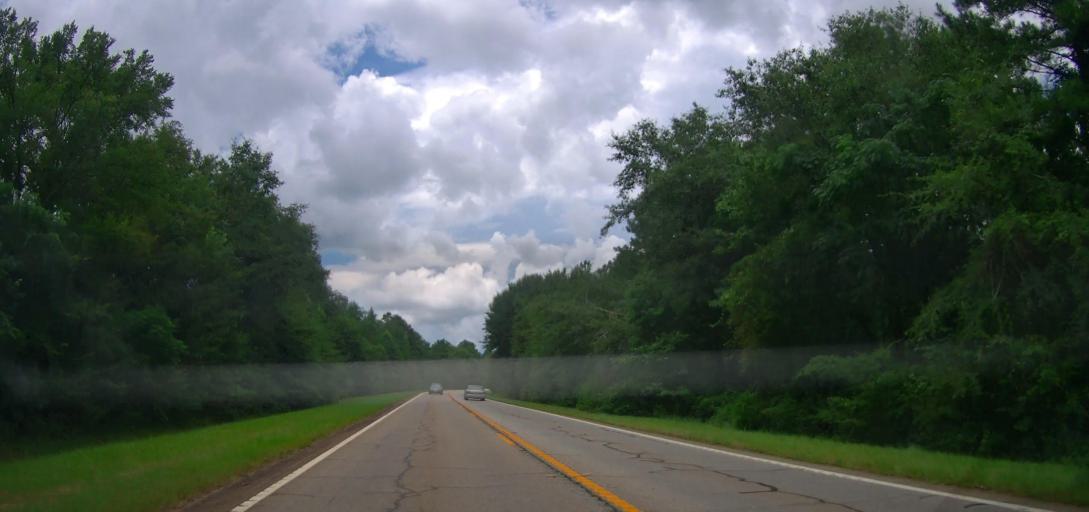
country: US
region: Georgia
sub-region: Pulaski County
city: Hawkinsville
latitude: 32.3477
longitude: -83.5334
